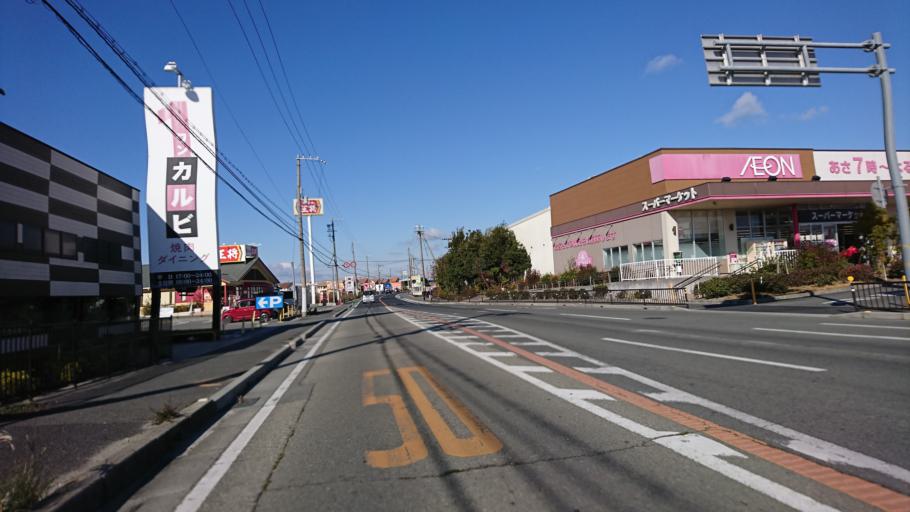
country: JP
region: Hyogo
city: Kakogawacho-honmachi
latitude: 34.7310
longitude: 134.8792
